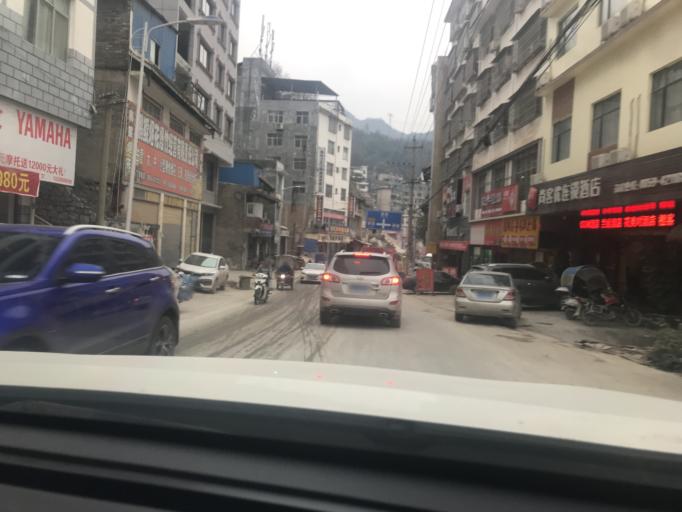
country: CN
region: Guangxi Zhuangzu Zizhiqu
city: Xinzhou
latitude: 24.9842
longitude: 105.8060
